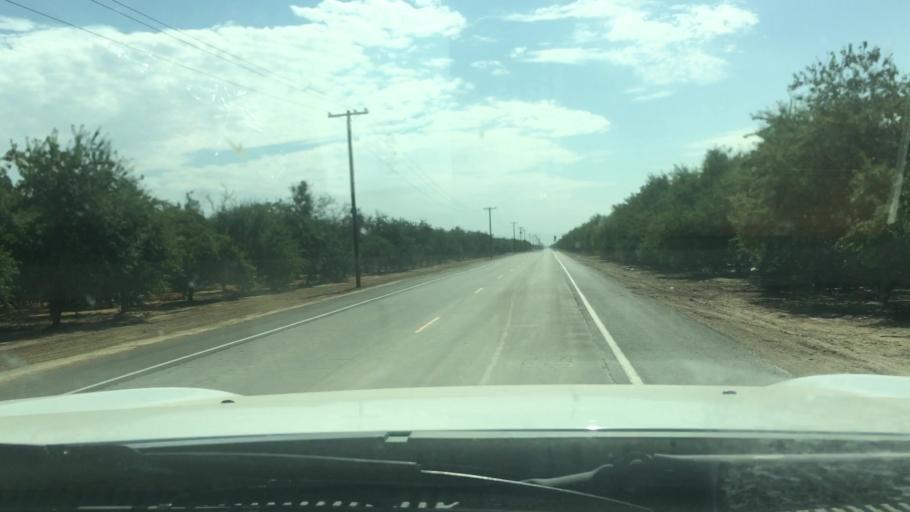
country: US
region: California
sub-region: Kern County
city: Wasco
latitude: 35.5577
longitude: -119.4651
